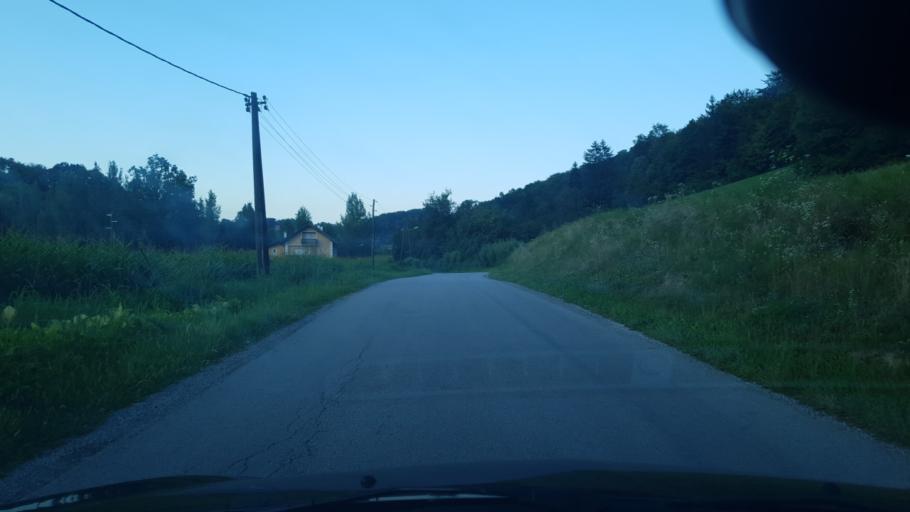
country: HR
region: Krapinsko-Zagorska
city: Zabok
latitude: 46.0237
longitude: 15.8900
